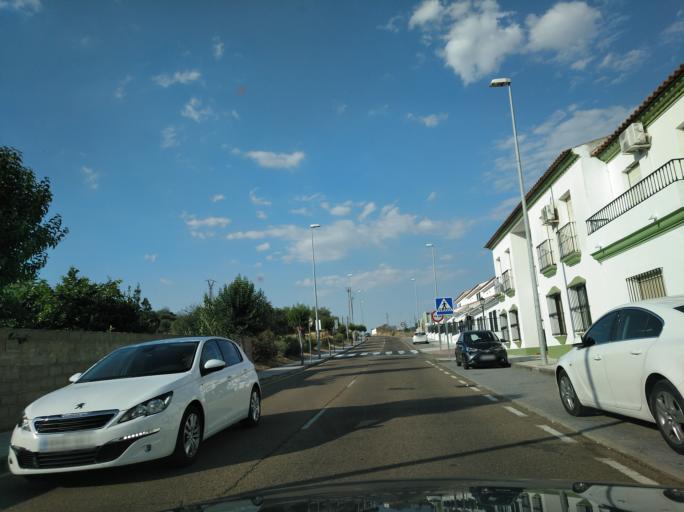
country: ES
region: Extremadura
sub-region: Provincia de Badajoz
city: Alconchel
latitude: 38.5184
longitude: -7.0665
